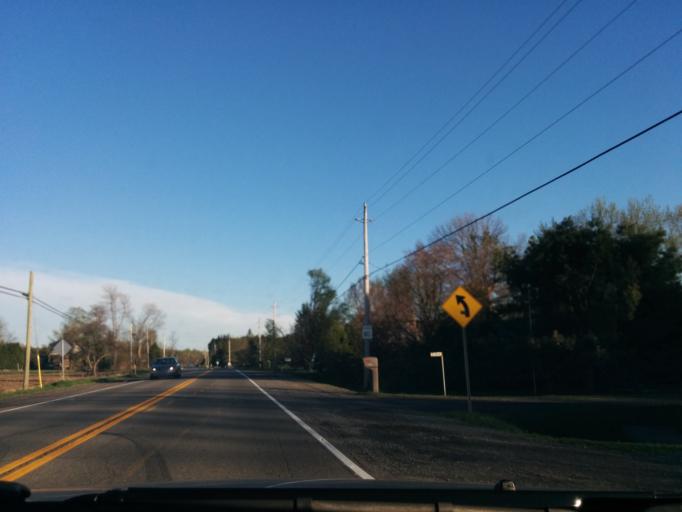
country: CA
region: Ontario
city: Ottawa
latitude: 45.1904
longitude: -75.6316
